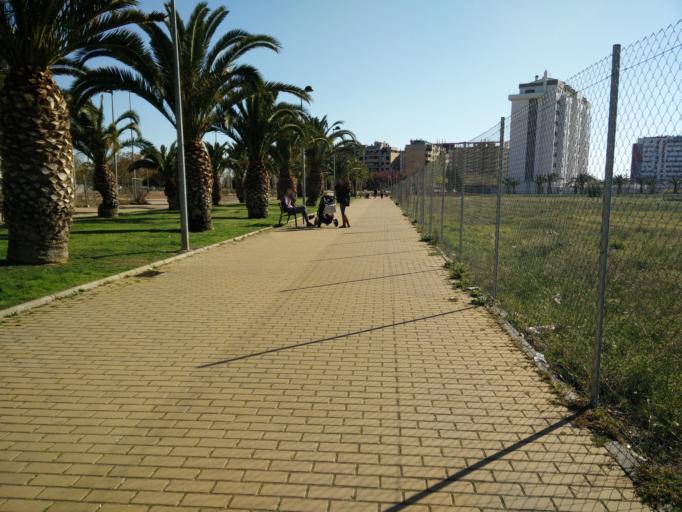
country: ES
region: Valencia
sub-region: Provincia de Castello
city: Castello de la Plana
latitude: 39.9771
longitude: -0.0378
